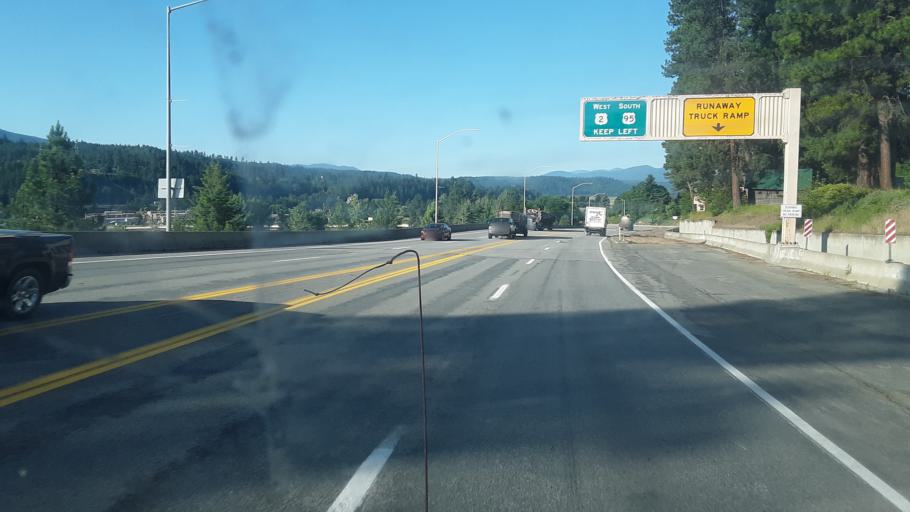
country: US
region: Idaho
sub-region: Boundary County
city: Bonners Ferry
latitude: 48.7050
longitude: -116.3115
